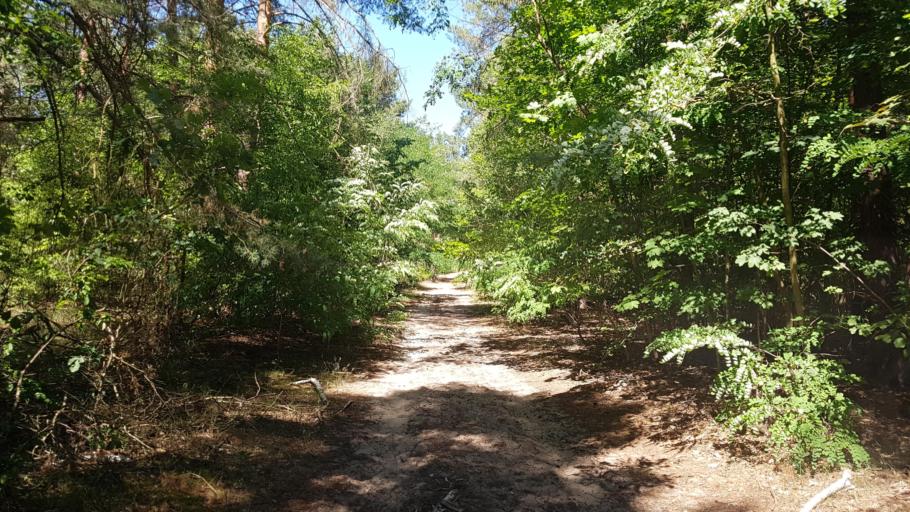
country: DE
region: Brandenburg
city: Trebbin
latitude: 52.2443
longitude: 13.1679
